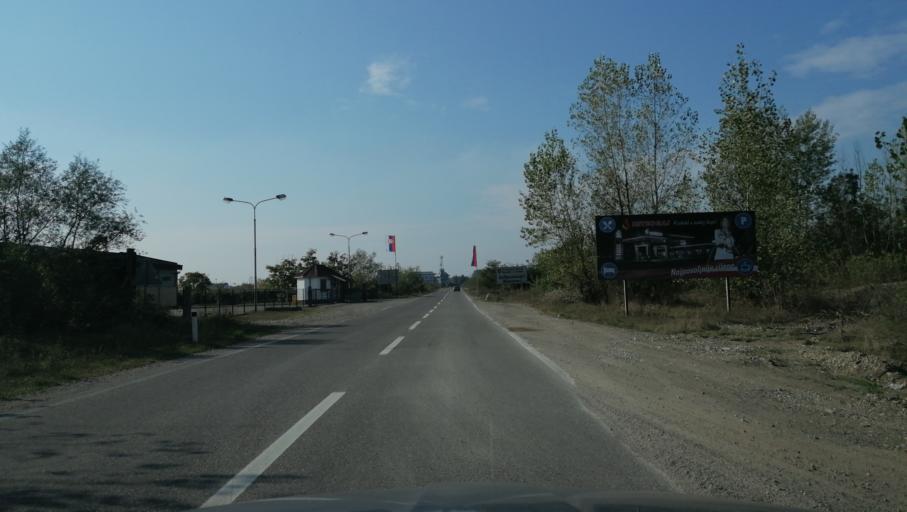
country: BA
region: Republika Srpska
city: Popovi
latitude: 44.7772
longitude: 19.3260
